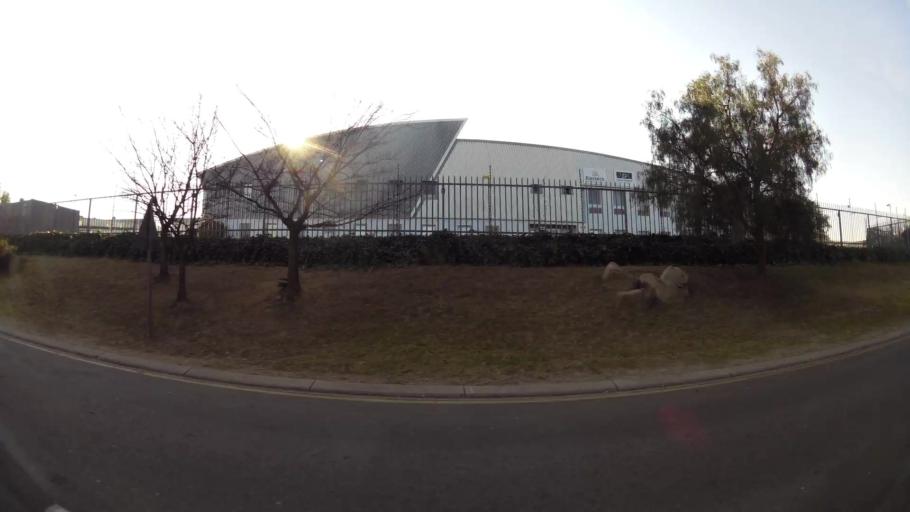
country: ZA
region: Gauteng
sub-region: City of Johannesburg Metropolitan Municipality
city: Modderfontein
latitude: -26.0685
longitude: 28.1125
